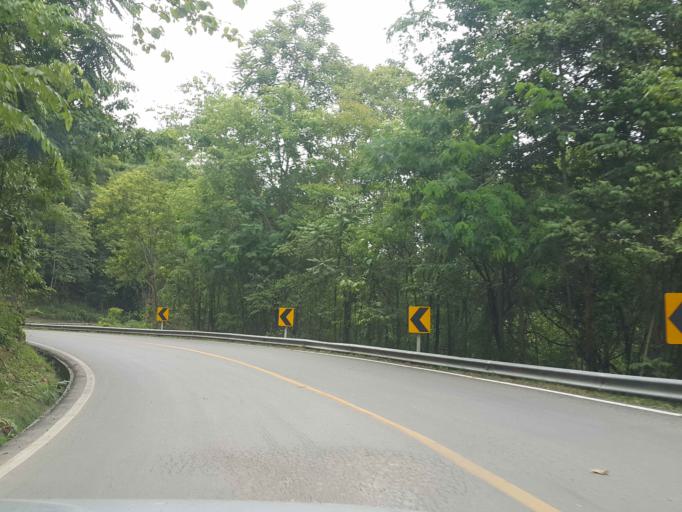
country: TH
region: Lampang
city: Thoen
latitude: 17.6742
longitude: 99.1064
